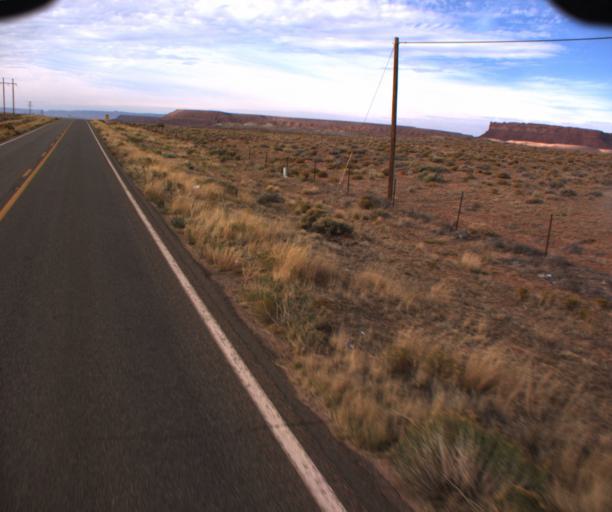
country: US
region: Arizona
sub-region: Apache County
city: Many Farms
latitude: 36.5043
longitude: -109.4785
